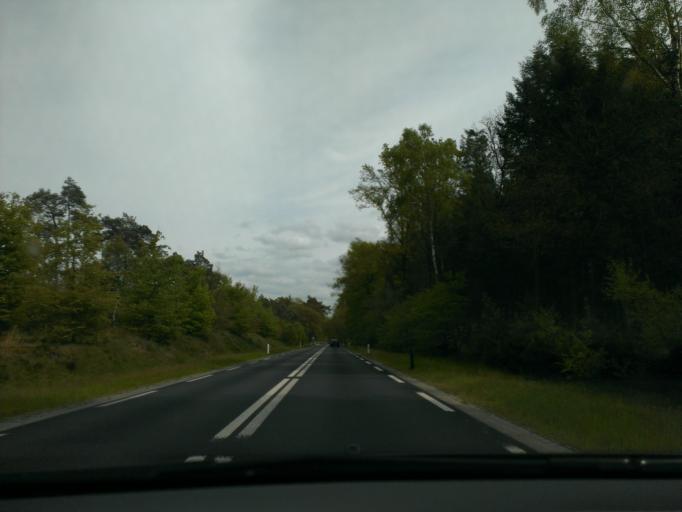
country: NL
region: Gelderland
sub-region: Gemeente Nunspeet
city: Nunspeet
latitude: 52.3609
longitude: 5.8615
